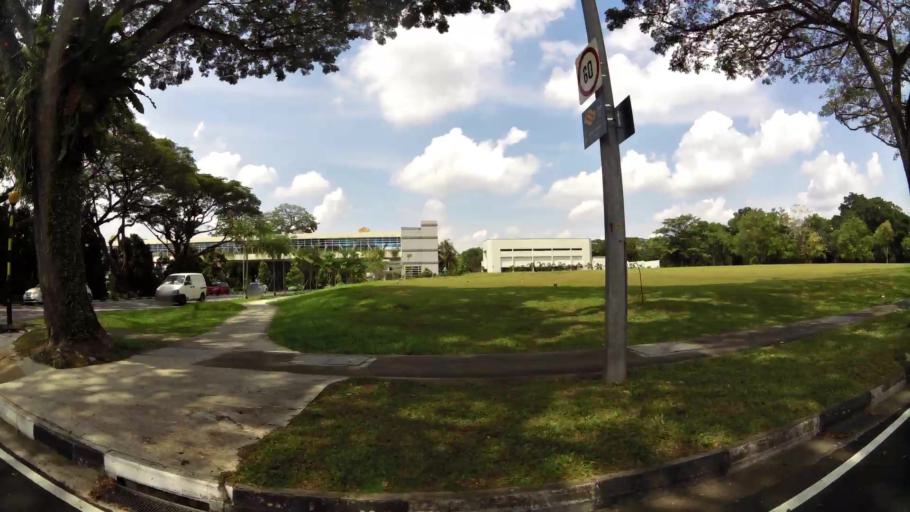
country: SG
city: Singapore
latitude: 1.3313
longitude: 103.7979
